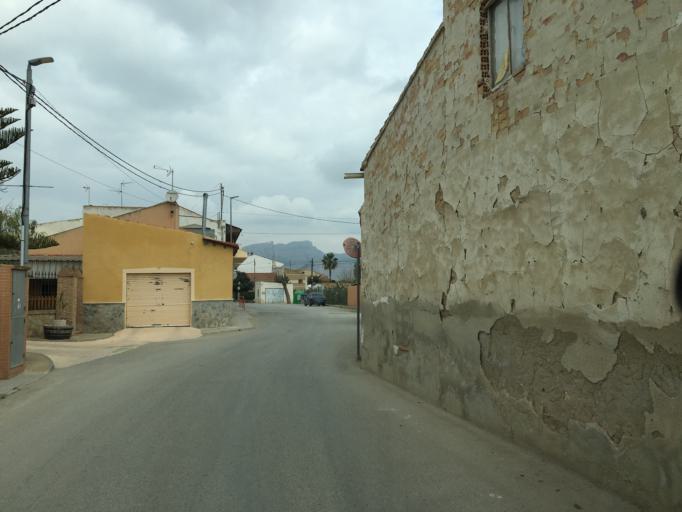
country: ES
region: Murcia
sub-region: Murcia
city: Beniel
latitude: 38.0385
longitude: -0.9880
